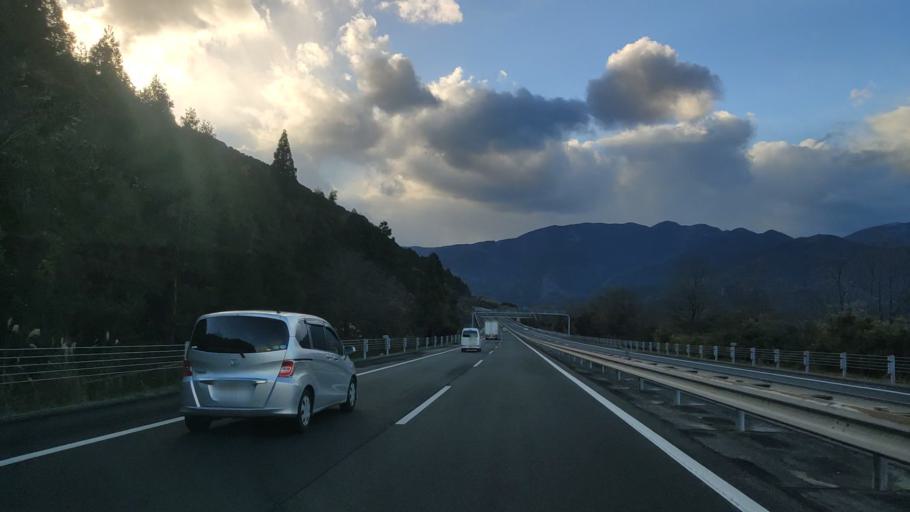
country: JP
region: Ehime
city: Saijo
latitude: 33.8560
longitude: 133.0348
